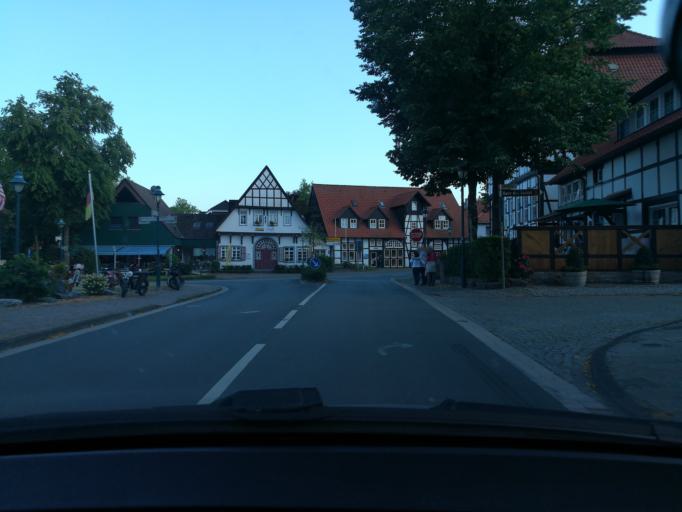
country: DE
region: North Rhine-Westphalia
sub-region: Regierungsbezirk Munster
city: Lienen
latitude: 52.1473
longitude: 7.9760
